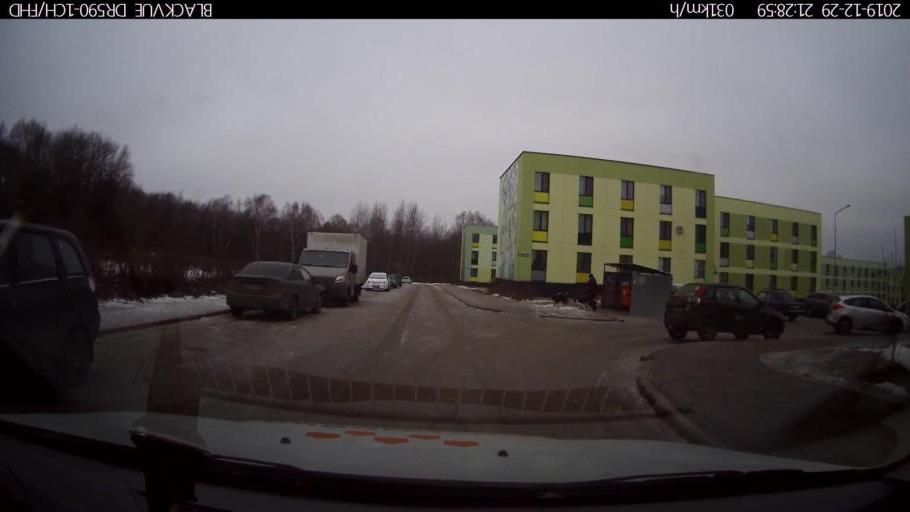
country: RU
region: Nizjnij Novgorod
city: Afonino
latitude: 56.2166
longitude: 44.0178
